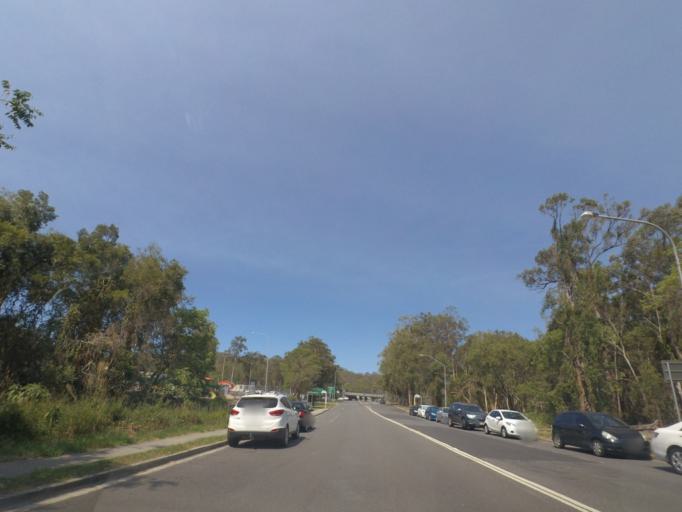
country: AU
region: Queensland
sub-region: Brisbane
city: Nathan
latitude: -27.5509
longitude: 153.0640
